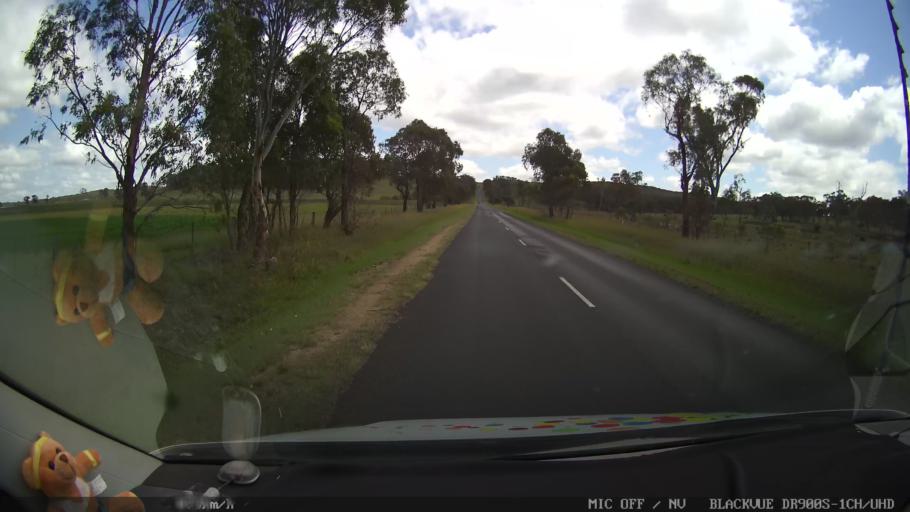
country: AU
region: New South Wales
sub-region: Glen Innes Severn
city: Glen Innes
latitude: -29.5978
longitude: 151.6663
